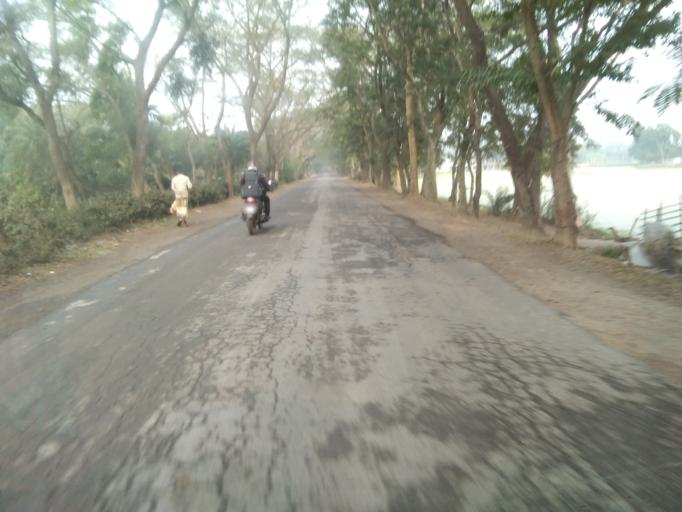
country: BD
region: Khulna
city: Satkhira
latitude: 22.6741
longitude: 89.0137
